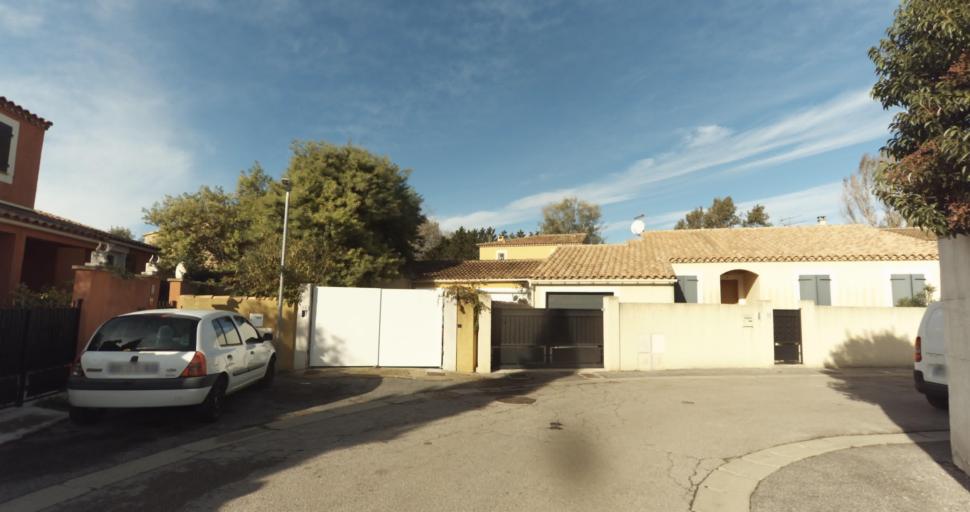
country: FR
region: Languedoc-Roussillon
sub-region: Departement du Gard
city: Aigues-Mortes
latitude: 43.5732
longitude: 4.1779
